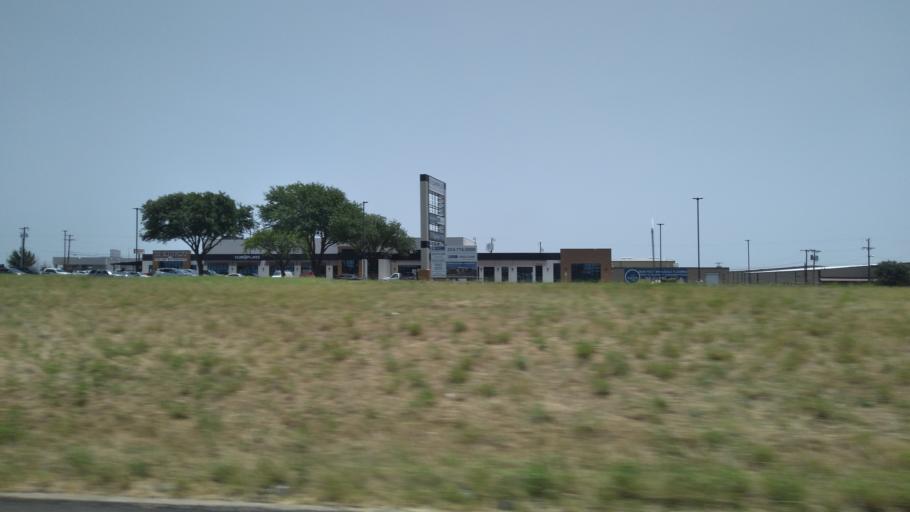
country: US
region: Texas
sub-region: McLennan County
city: Woodway
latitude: 31.5111
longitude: -97.1912
